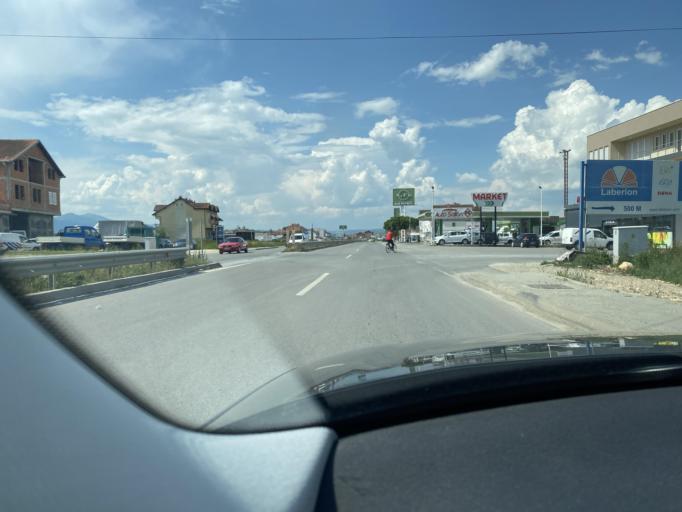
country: XK
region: Pristina
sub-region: Podujevo
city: Podujeva
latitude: 42.8791
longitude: 21.1814
